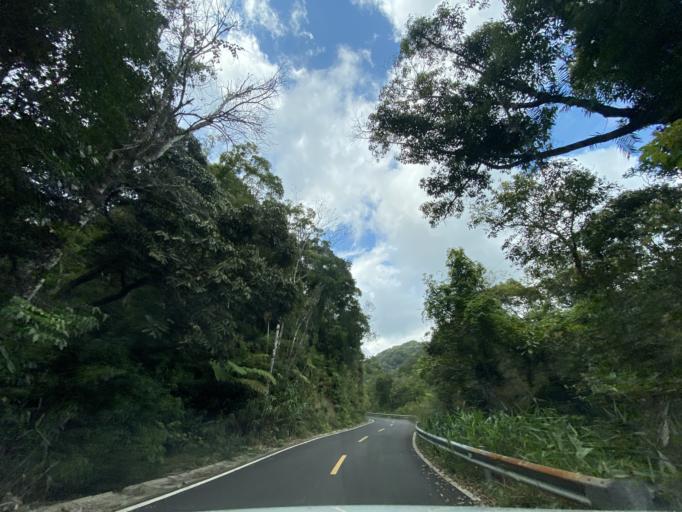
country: CN
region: Hainan
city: Benhao
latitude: 18.6969
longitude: 109.8792
